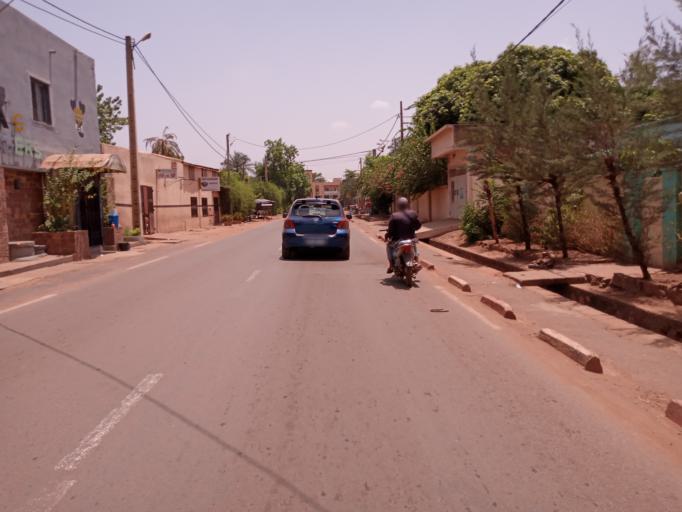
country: ML
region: Bamako
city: Bamako
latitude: 12.6465
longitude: -7.9775
